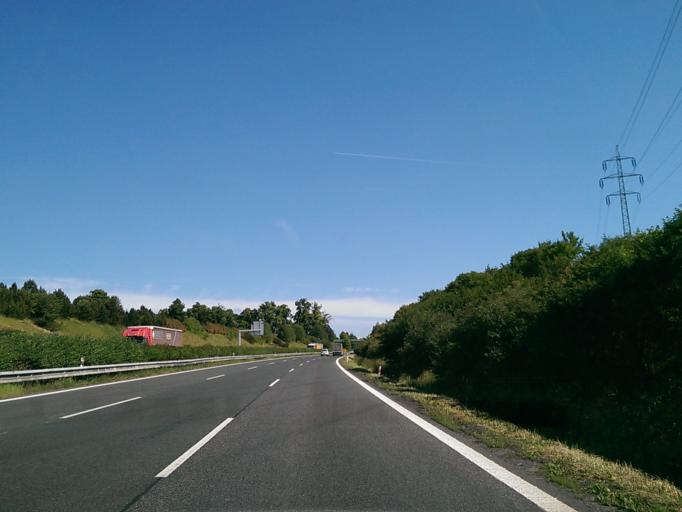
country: CZ
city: Ohrazenice
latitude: 50.6231
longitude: 15.1087
